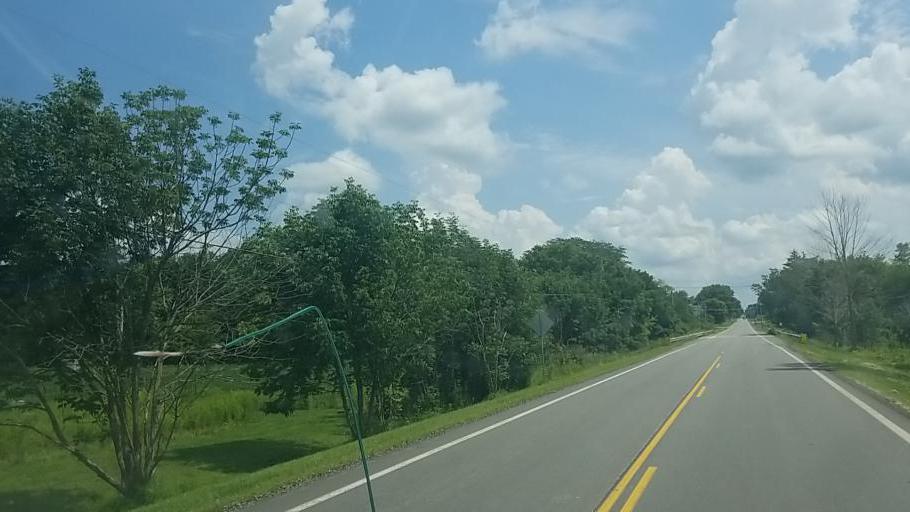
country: US
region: Ohio
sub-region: Medina County
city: Lodi
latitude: 41.1003
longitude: -82.0788
